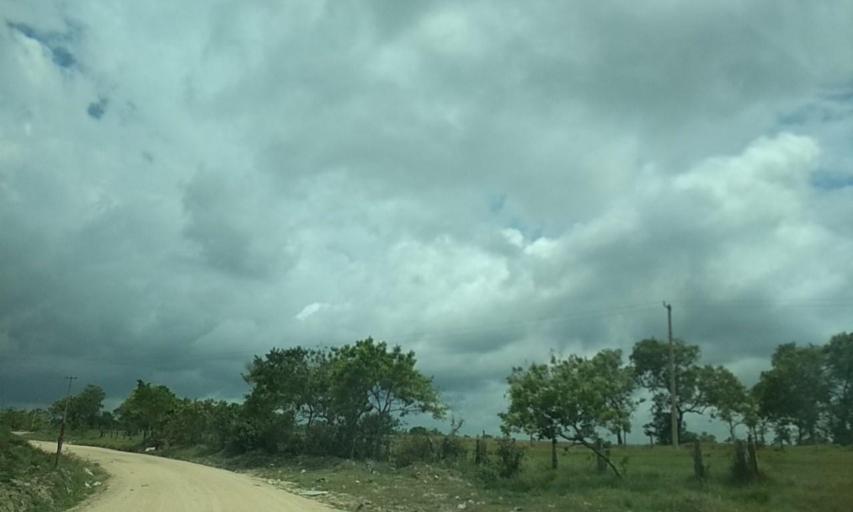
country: MX
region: Veracruz
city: Las Choapas
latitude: 17.9021
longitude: -94.1238
